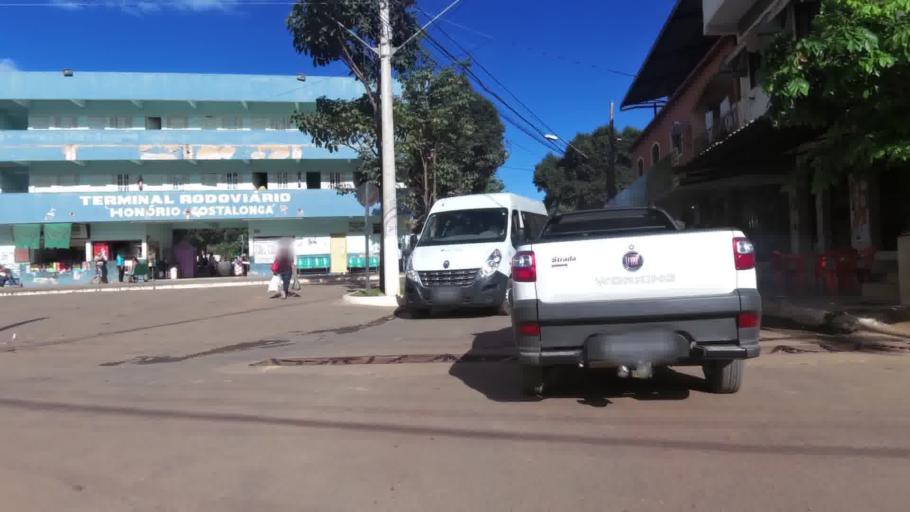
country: BR
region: Espirito Santo
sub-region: Marataizes
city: Marataizes
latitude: -21.0996
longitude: -41.0456
